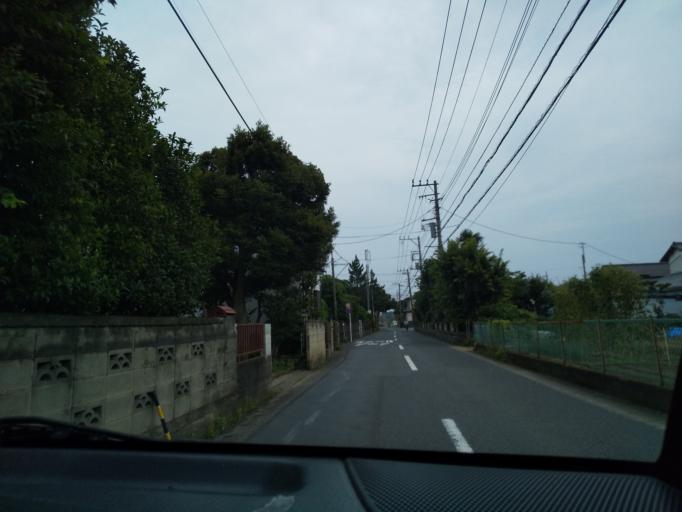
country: JP
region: Kanagawa
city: Atsugi
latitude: 35.3954
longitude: 139.3849
